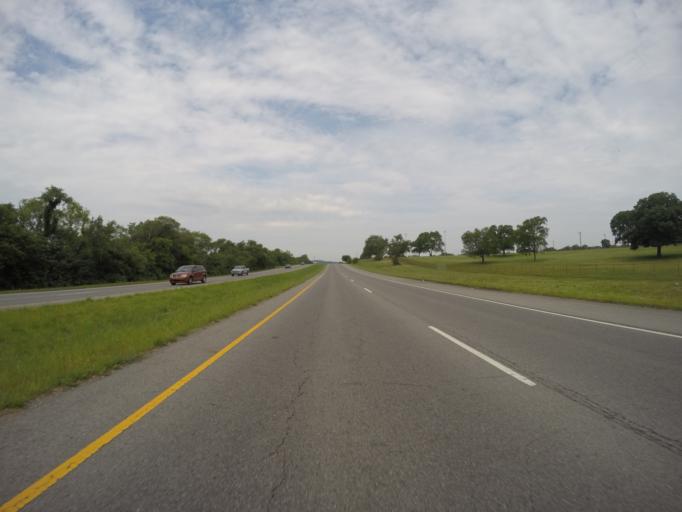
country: US
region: Tennessee
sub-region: Davidson County
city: Goodlettsville
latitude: 36.2643
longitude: -86.6986
